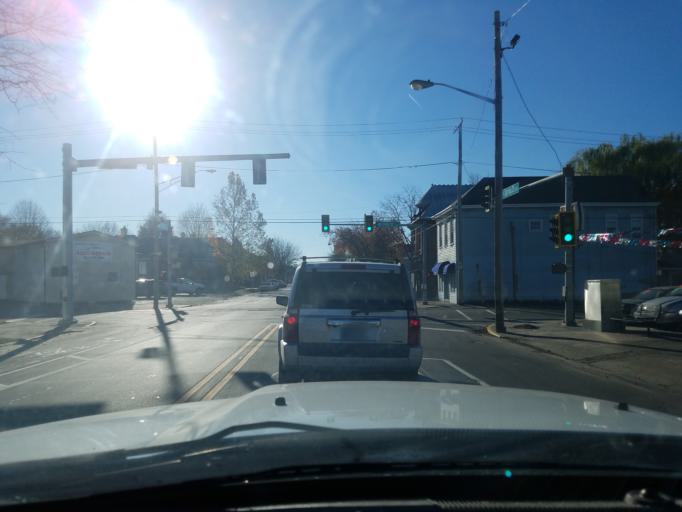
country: US
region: Indiana
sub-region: Floyd County
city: New Albany
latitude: 38.2917
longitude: -85.8090
